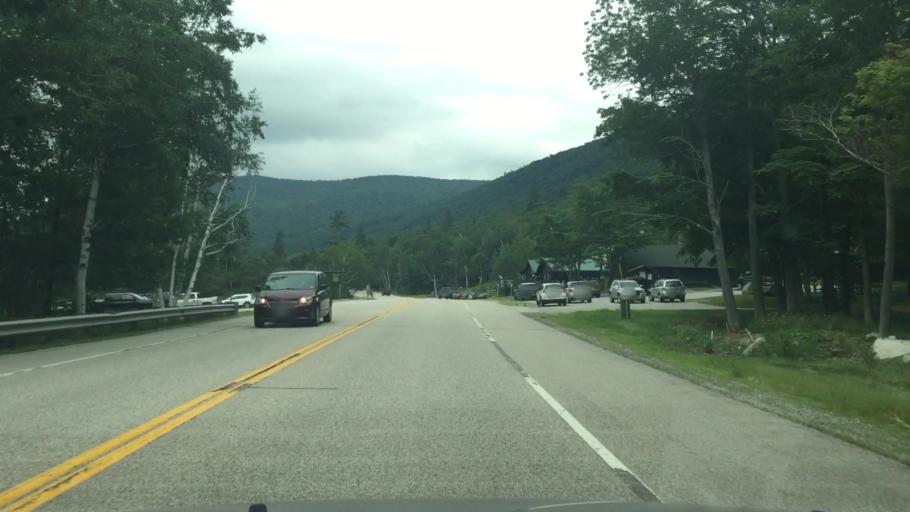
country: US
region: New Hampshire
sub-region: Grafton County
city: Deerfield
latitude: 44.1833
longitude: -71.3995
